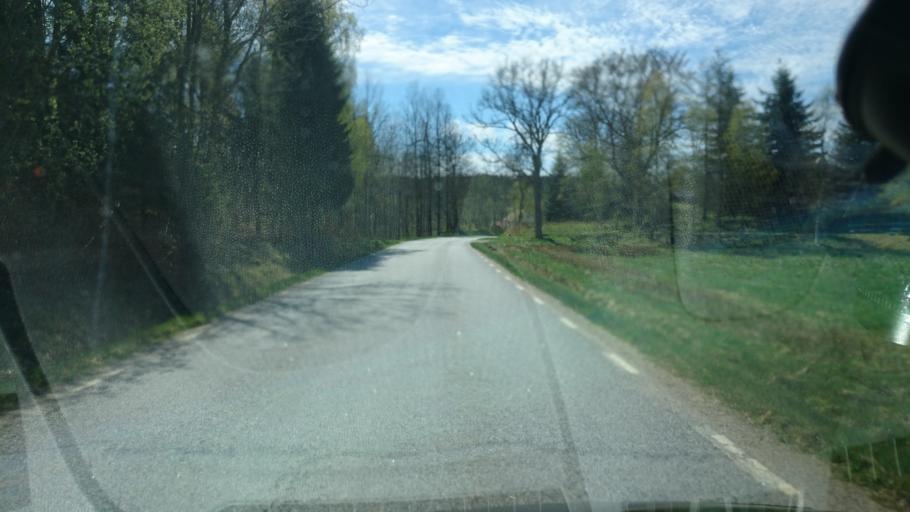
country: SE
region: Vaestra Goetaland
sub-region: Munkedals Kommun
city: Munkedal
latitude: 58.4173
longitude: 11.6854
